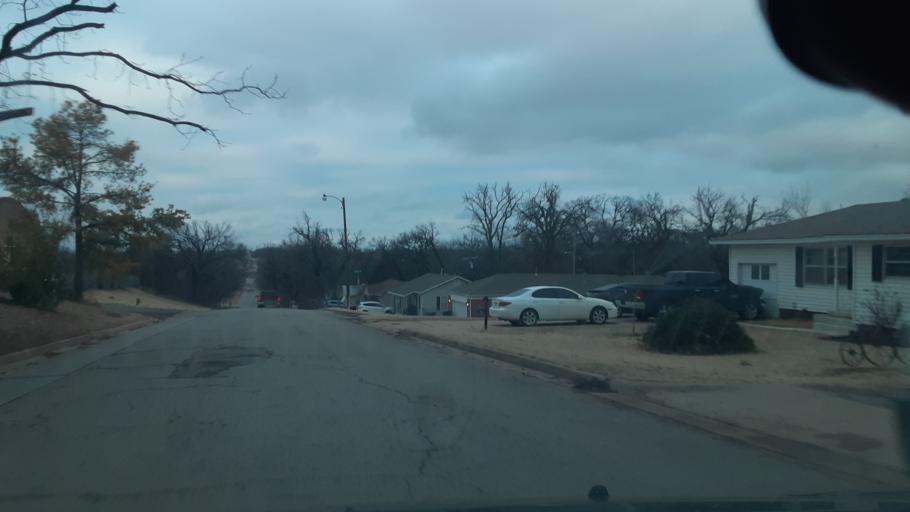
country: US
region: Oklahoma
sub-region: Logan County
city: Guthrie
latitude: 35.8828
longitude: -97.4164
